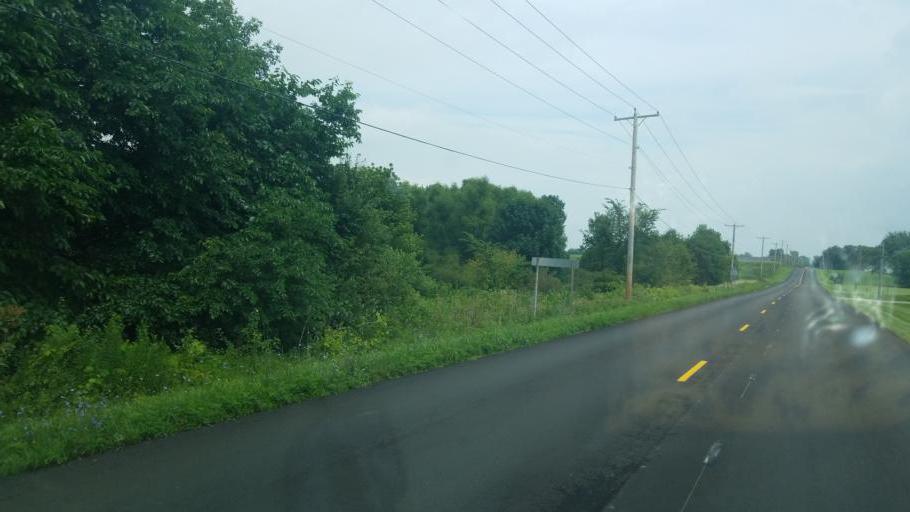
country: US
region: Ohio
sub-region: Logan County
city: Russells Point
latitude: 40.4703
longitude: -83.8538
